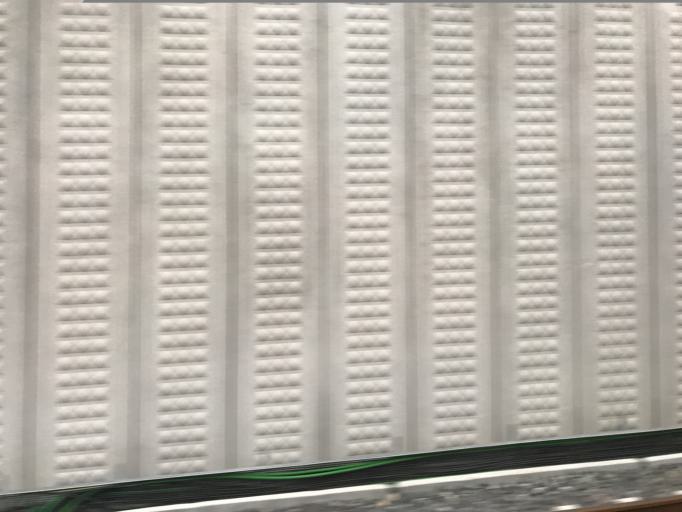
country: TR
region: Istanbul
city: UEskuedar
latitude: 40.9959
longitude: 29.0313
